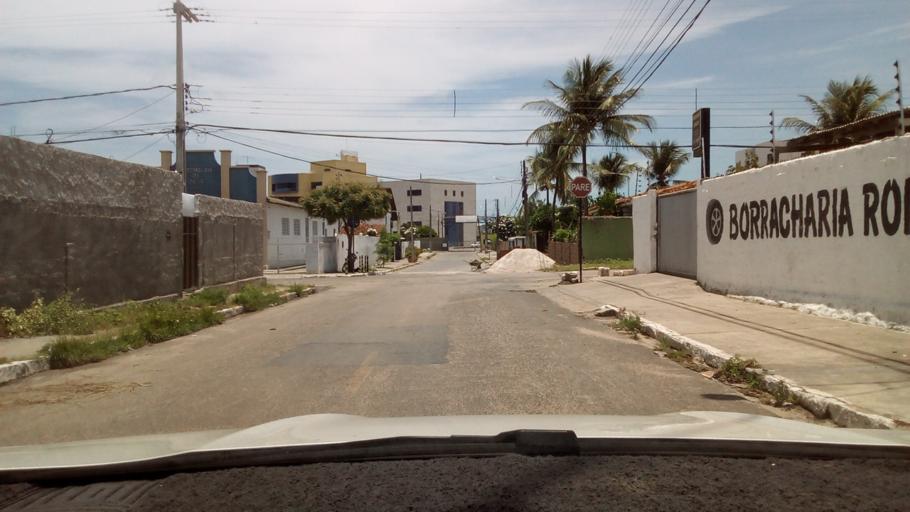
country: BR
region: Paraiba
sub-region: Joao Pessoa
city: Joao Pessoa
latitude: -7.1689
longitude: -34.8691
